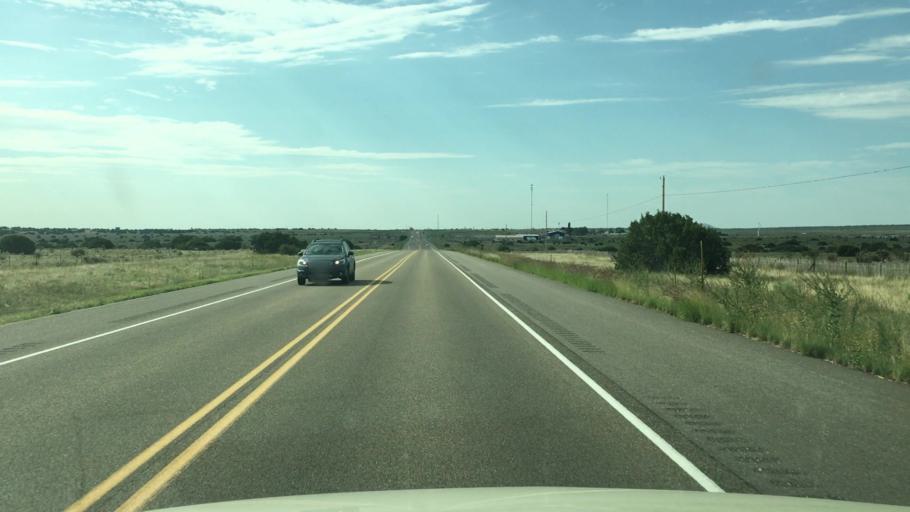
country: US
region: New Mexico
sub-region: Torrance County
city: Moriarty
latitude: 35.0244
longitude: -105.6733
